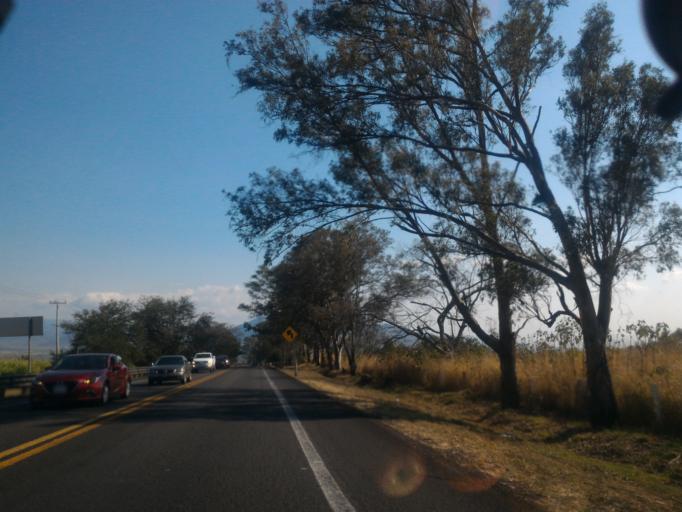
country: MX
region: Jalisco
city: Tuxpan
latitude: 19.5602
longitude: -103.4405
